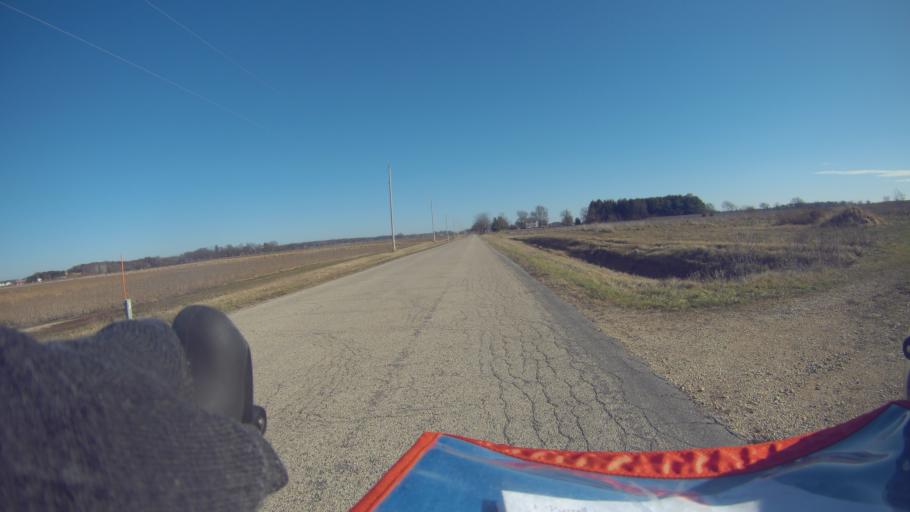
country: US
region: Wisconsin
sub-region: Green County
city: Brooklyn
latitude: 42.8708
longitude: -89.4045
